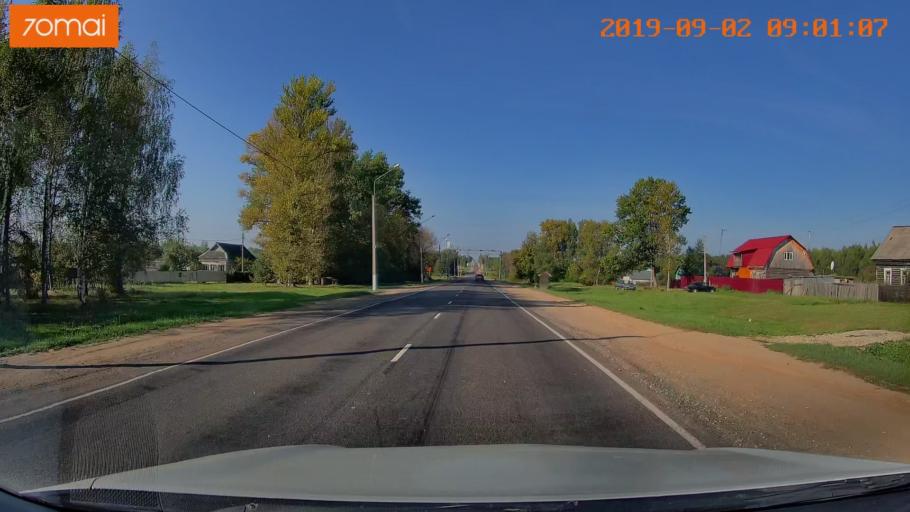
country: RU
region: Kaluga
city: Myatlevo
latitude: 54.9080
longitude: 35.6932
